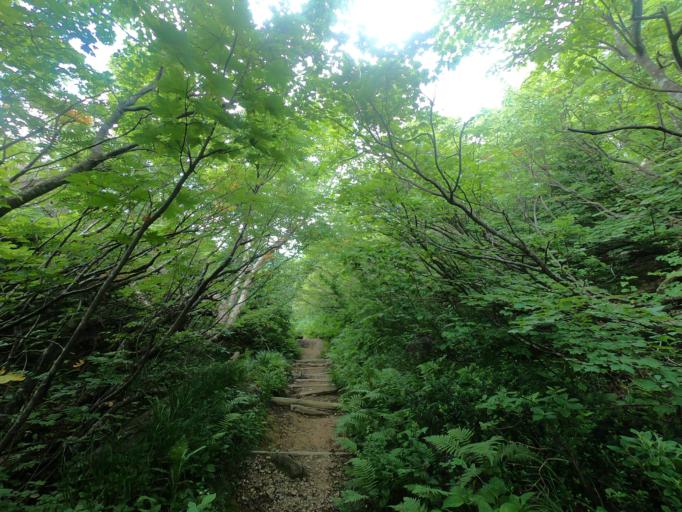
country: JP
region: Akita
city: Yuzawa
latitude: 38.9772
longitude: 140.7732
